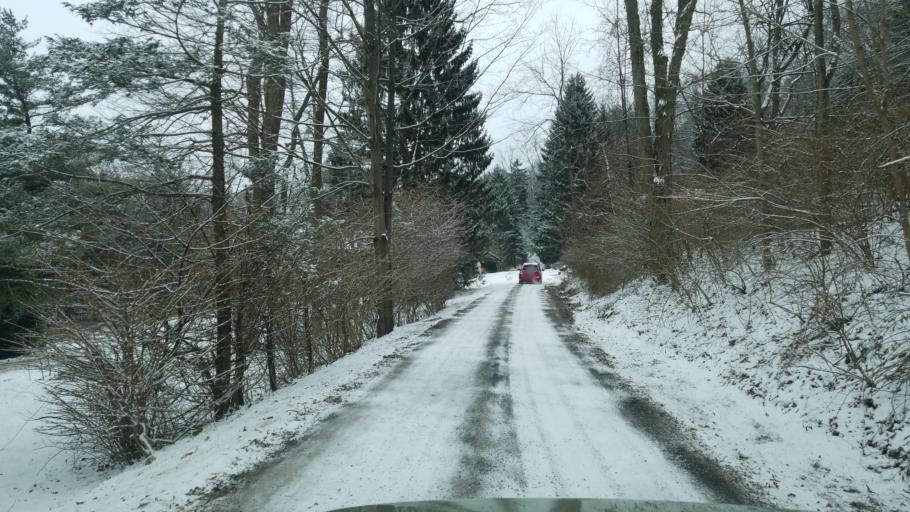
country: US
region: Pennsylvania
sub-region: Centre County
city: Centre Hall
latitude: 40.7695
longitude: -77.6789
